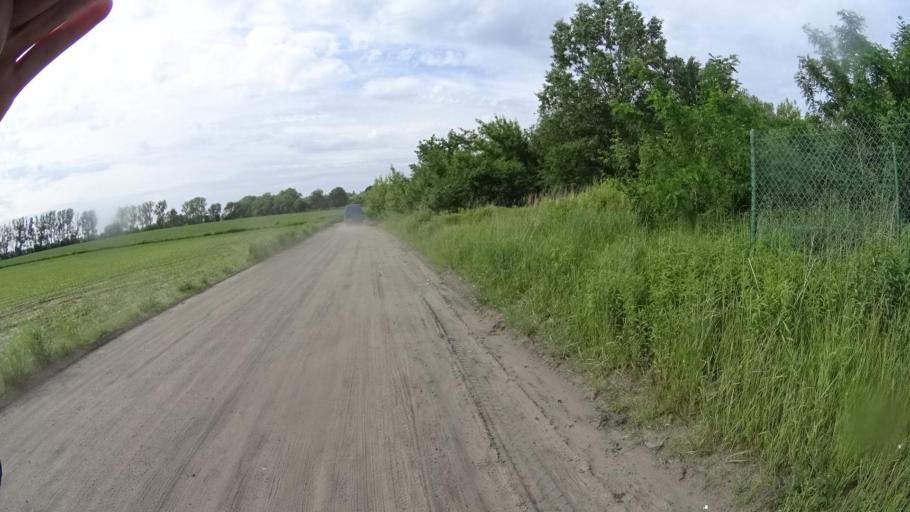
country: PL
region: Masovian Voivodeship
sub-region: Powiat warszawski zachodni
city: Jozefow
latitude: 52.1947
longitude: 20.7422
